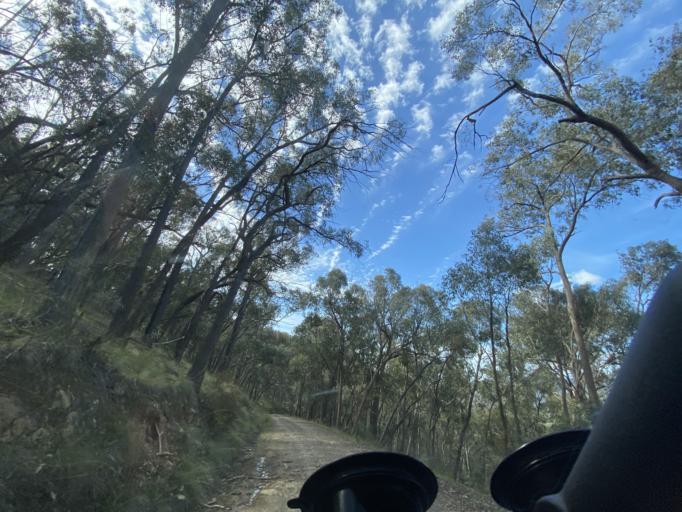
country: AU
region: Victoria
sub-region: Mansfield
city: Mansfield
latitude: -36.7996
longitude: 146.1124
